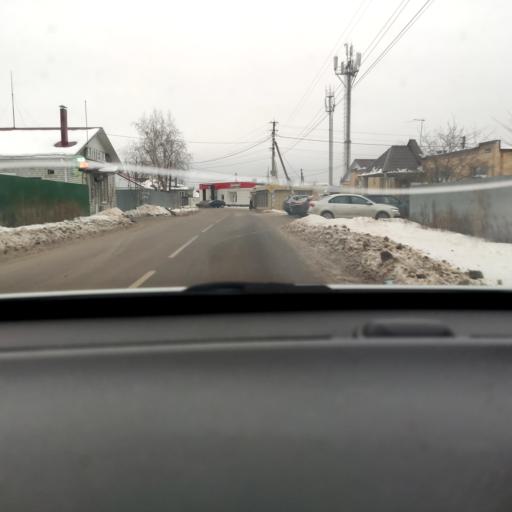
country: RU
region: Voronezj
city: Somovo
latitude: 51.7461
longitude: 39.3397
